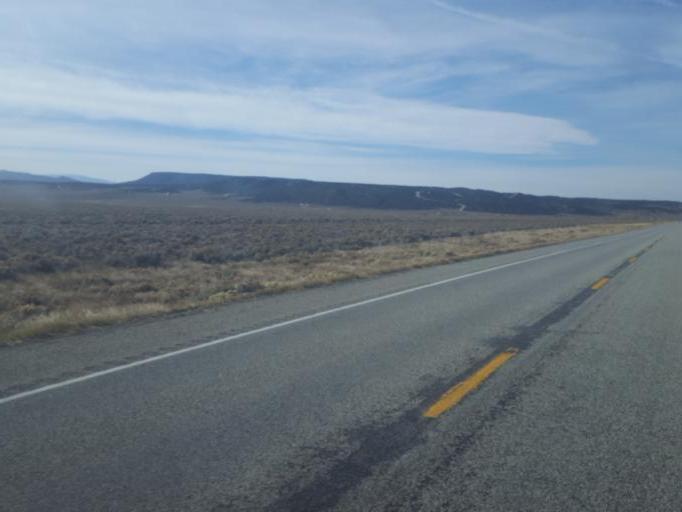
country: US
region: Colorado
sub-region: Costilla County
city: San Luis
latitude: 37.4437
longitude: -105.3795
